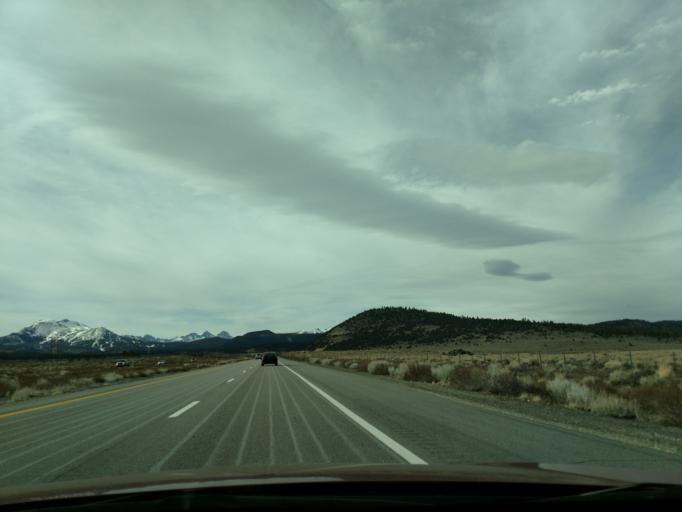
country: US
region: California
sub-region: Mono County
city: Mammoth Lakes
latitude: 37.6310
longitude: -118.8700
